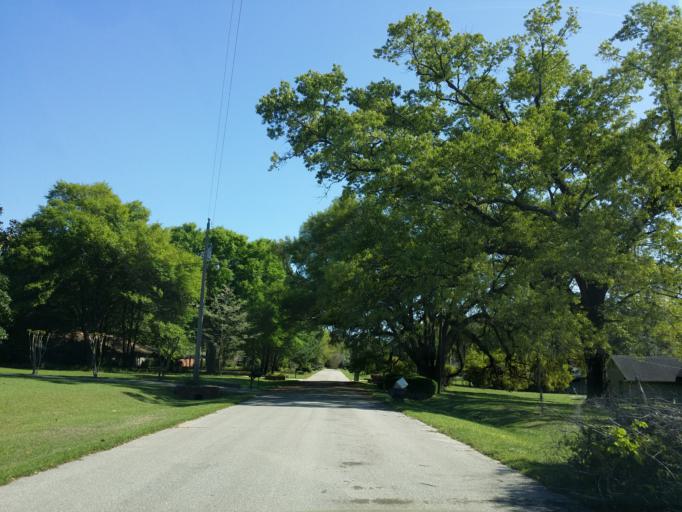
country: US
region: Florida
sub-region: Leon County
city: Tallahassee
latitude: 30.4834
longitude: -84.1862
